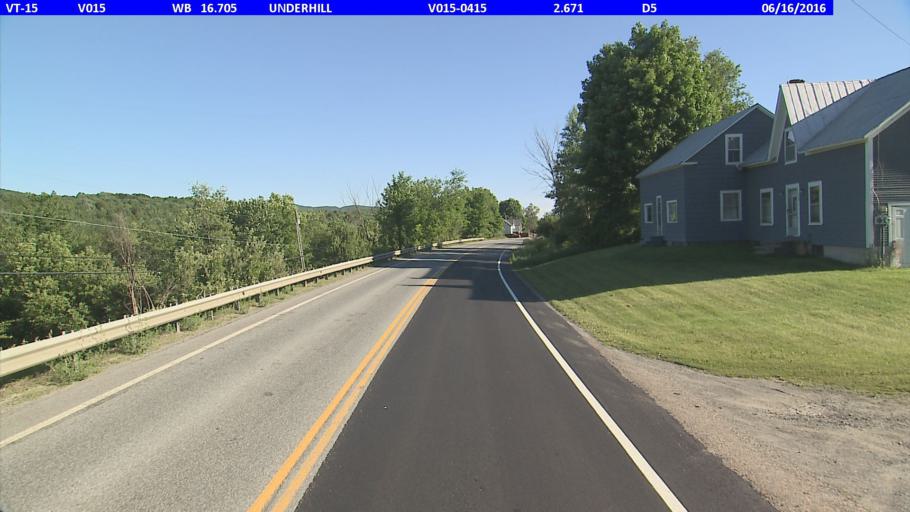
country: US
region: Vermont
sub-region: Chittenden County
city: Jericho
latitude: 44.5622
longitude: -72.9422
